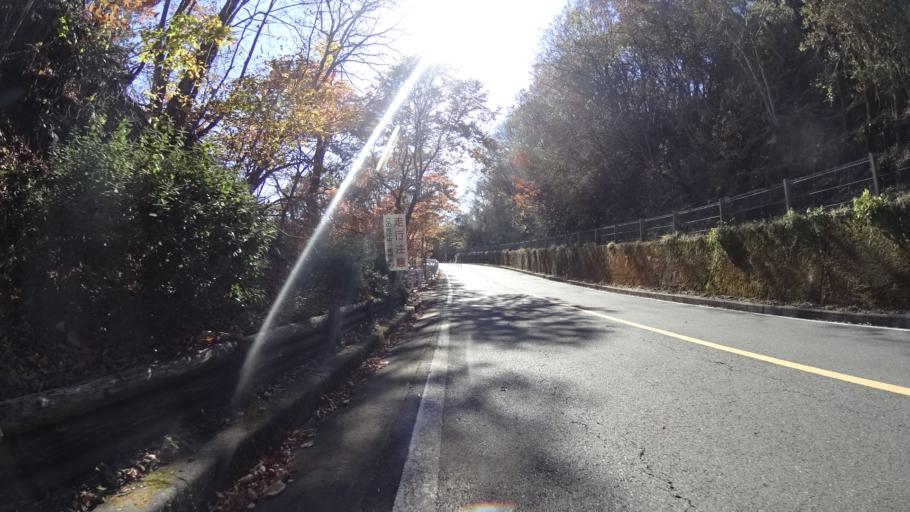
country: JP
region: Yamanashi
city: Uenohara
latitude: 35.7546
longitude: 139.0426
